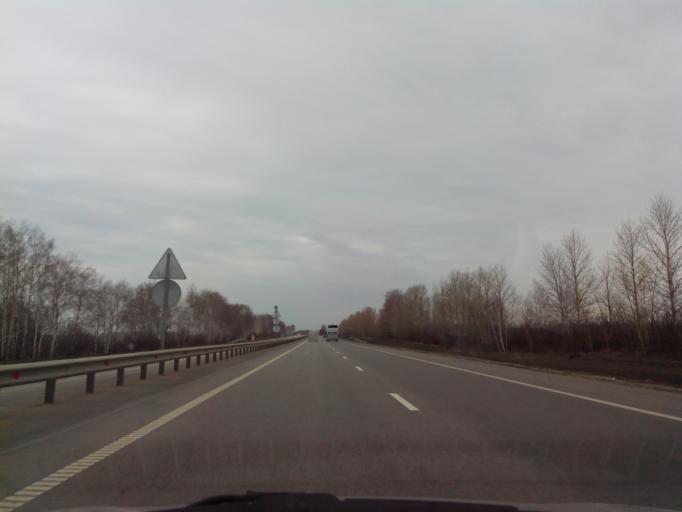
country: RU
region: Tambov
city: Selezni
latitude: 52.8087
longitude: 40.9608
